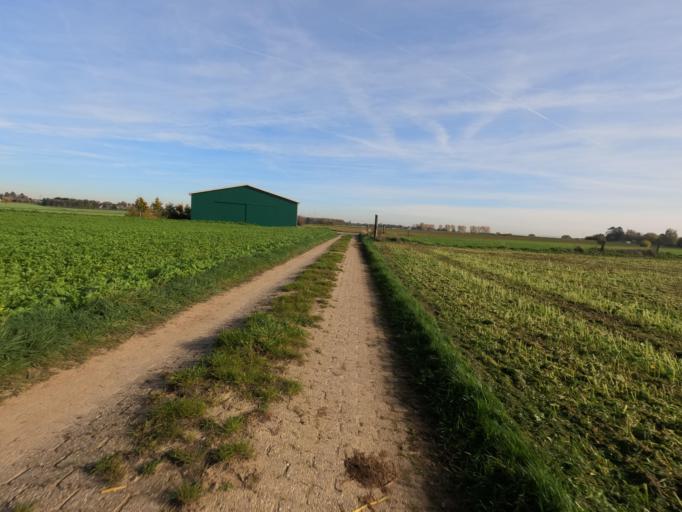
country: DE
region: North Rhine-Westphalia
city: Erkelenz
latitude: 51.0760
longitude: 6.3849
